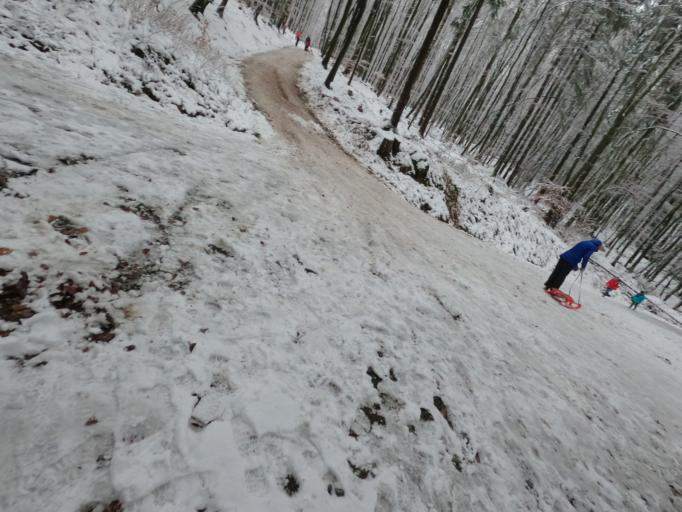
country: DE
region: Hesse
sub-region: Regierungsbezirk Darmstadt
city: Glashutten
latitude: 50.2227
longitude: 8.4254
